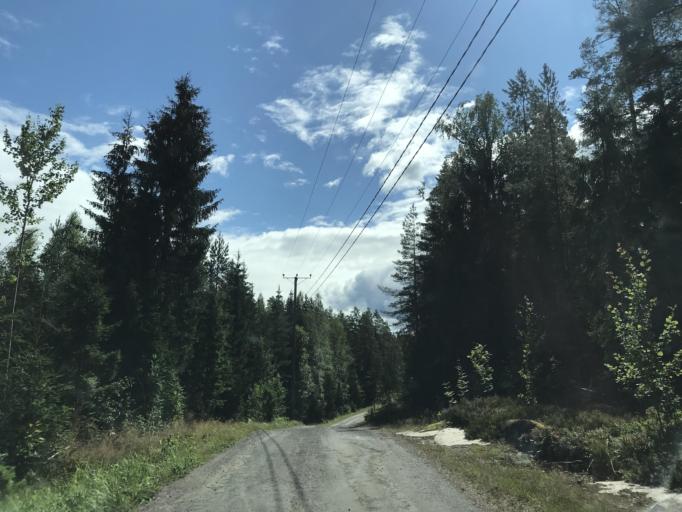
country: FI
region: Haeme
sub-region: Forssa
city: Tammela
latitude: 60.6299
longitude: 23.7557
